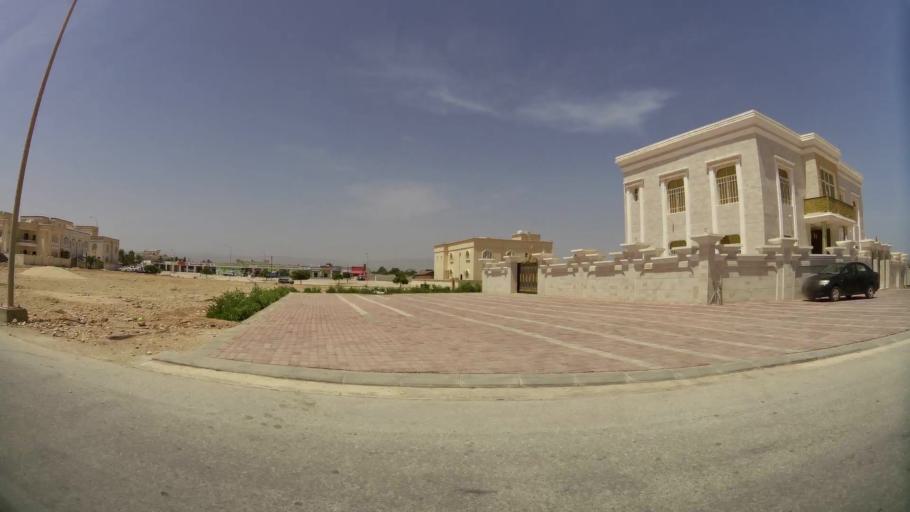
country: OM
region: Zufar
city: Salalah
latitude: 17.0591
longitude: 54.1617
